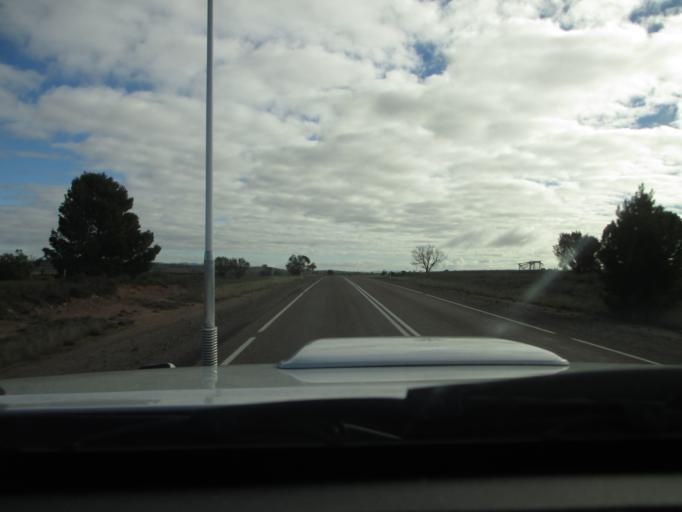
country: AU
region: South Australia
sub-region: Peterborough
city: Peterborough
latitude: -32.5527
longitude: 138.5610
